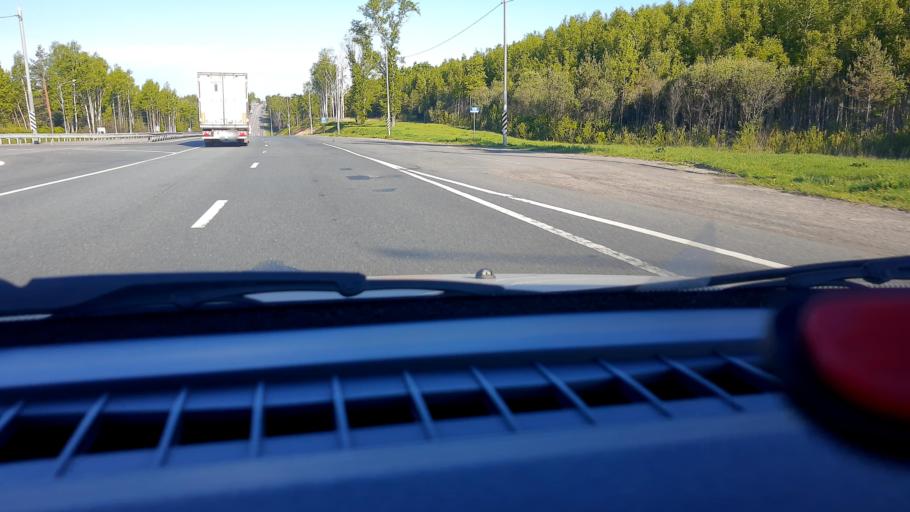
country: RU
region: Vladimir
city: Gorokhovets
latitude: 56.1672
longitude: 42.4662
